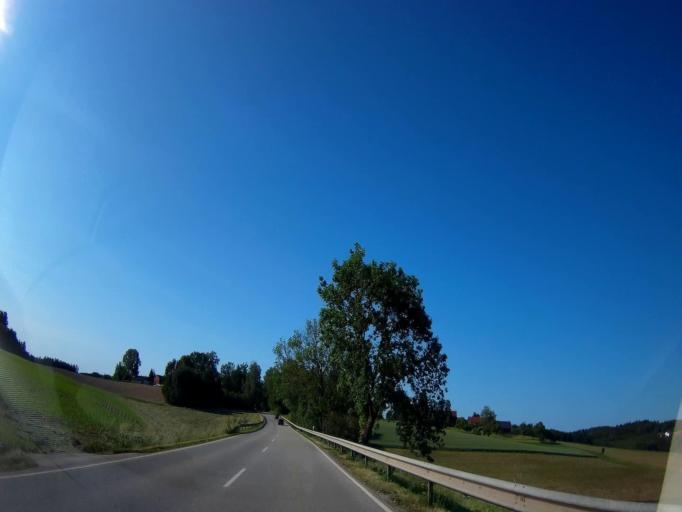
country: DE
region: Bavaria
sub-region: Lower Bavaria
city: Zeilarn
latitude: 48.3238
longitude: 12.8291
